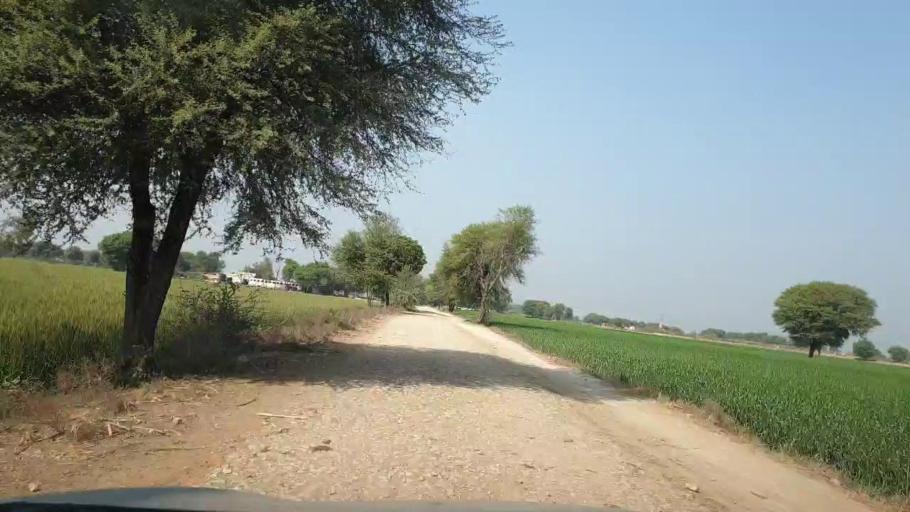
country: PK
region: Sindh
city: Bhit Shah
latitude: 25.7487
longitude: 68.4572
